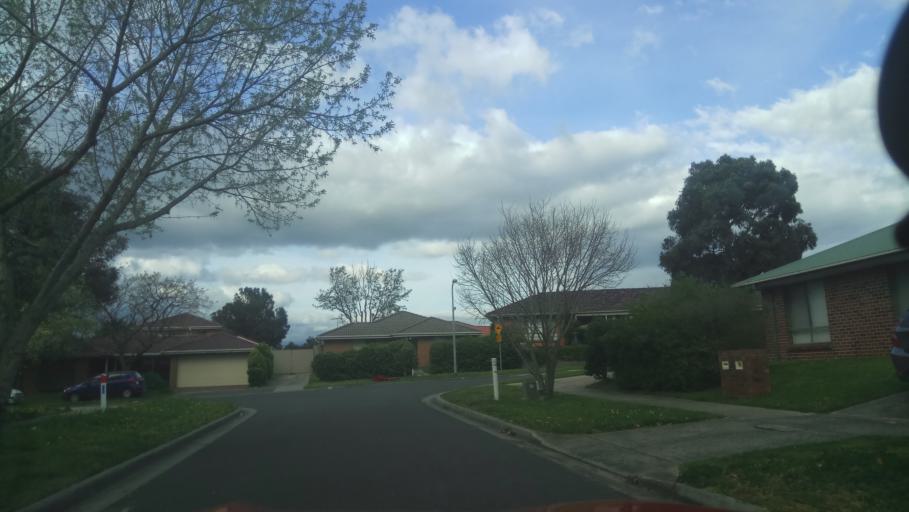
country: AU
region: Victoria
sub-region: Casey
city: Cranbourne North
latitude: -38.0691
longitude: 145.2701
